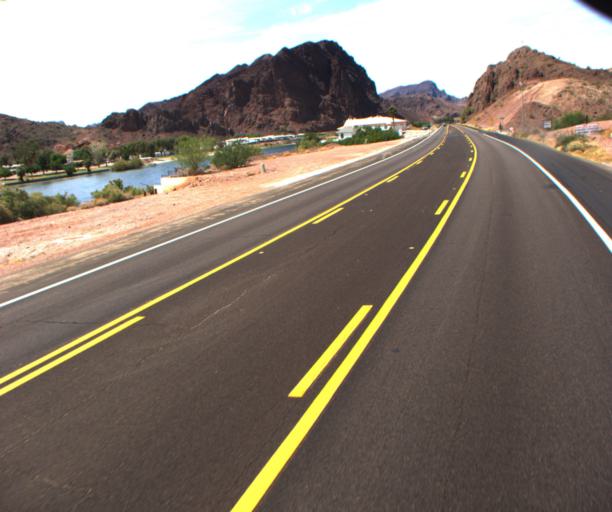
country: US
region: Arizona
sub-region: La Paz County
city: Cienega Springs
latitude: 34.2640
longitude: -114.1298
